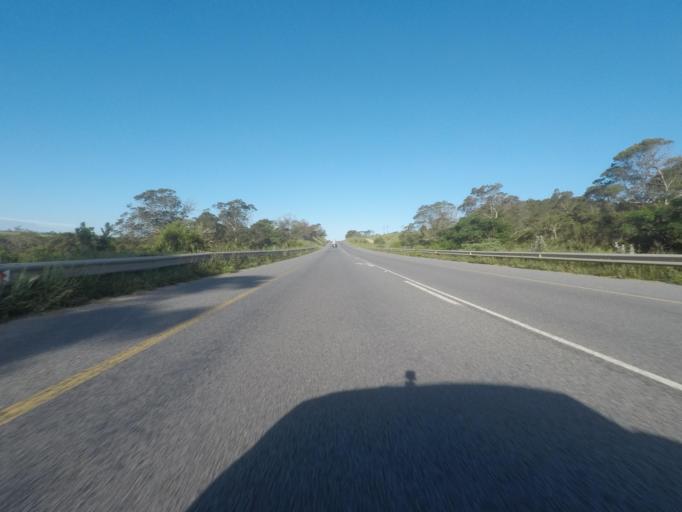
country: ZA
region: Eastern Cape
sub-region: Buffalo City Metropolitan Municipality
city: East London
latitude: -33.0590
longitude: 27.7930
